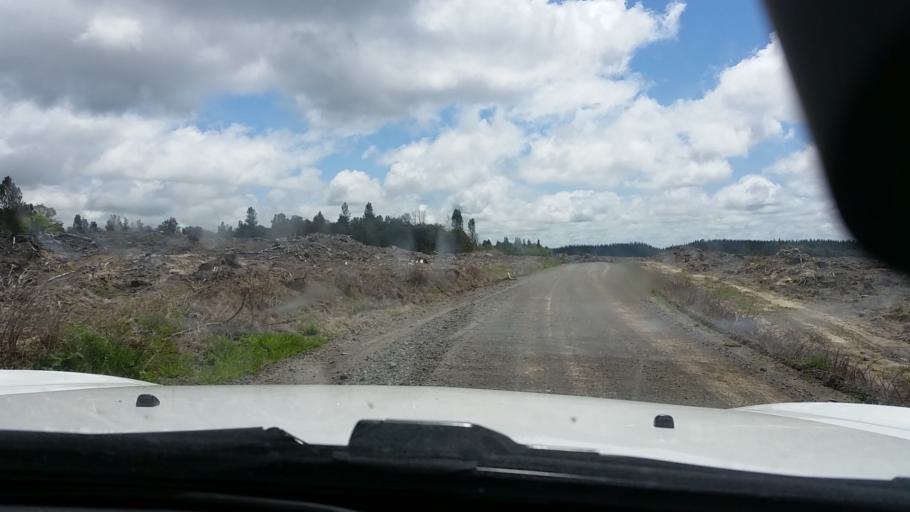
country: NZ
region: Bay of Plenty
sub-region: Kawerau District
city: Kawerau
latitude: -37.9984
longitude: 176.5407
